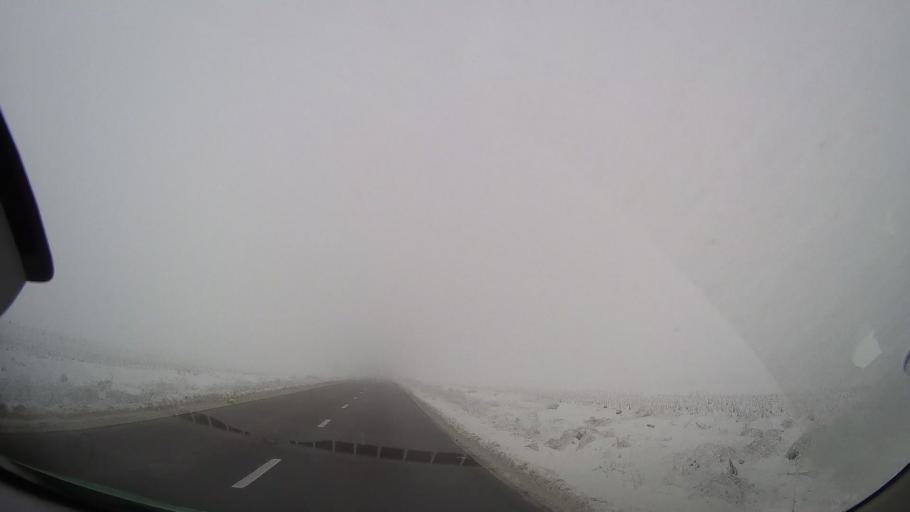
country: RO
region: Neamt
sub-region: Comuna Sabaoani
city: Sabaoani
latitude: 47.0365
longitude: 26.8541
